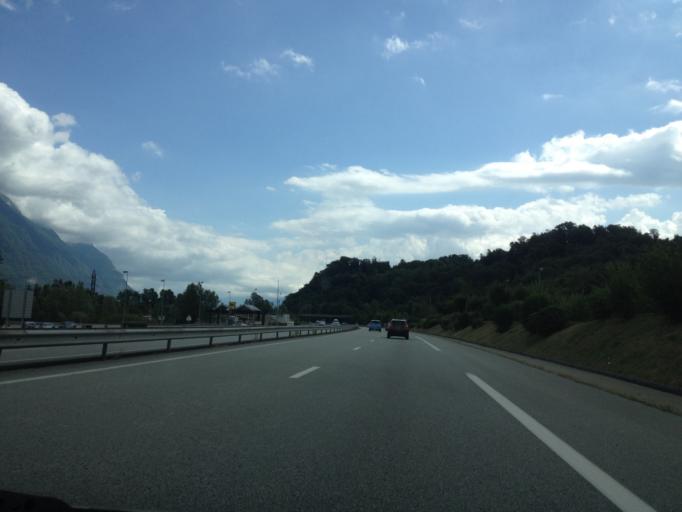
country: FR
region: Rhone-Alpes
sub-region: Departement de la Savoie
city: Coise-Saint-Jean-Pied-Gauthier
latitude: 45.5479
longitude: 6.1568
